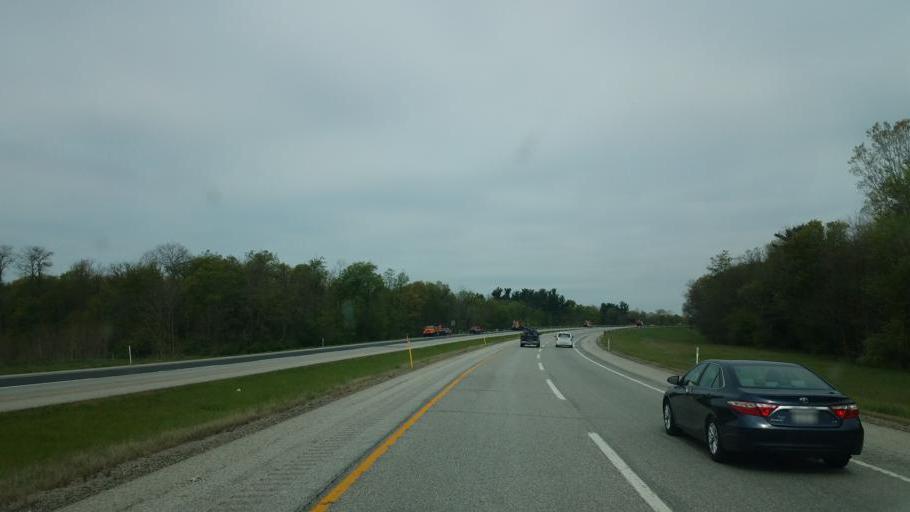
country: US
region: Indiana
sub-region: Elkhart County
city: Bristol
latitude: 41.7290
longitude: -85.7713
